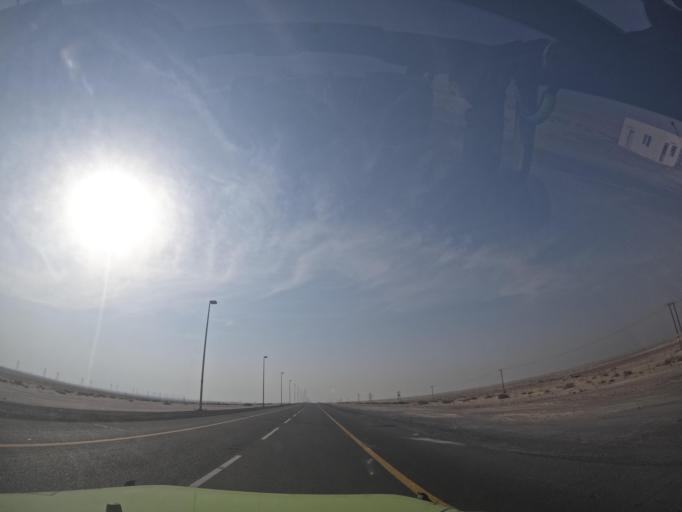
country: AE
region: Dubai
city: Dubai
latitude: 24.7613
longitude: 55.0976
